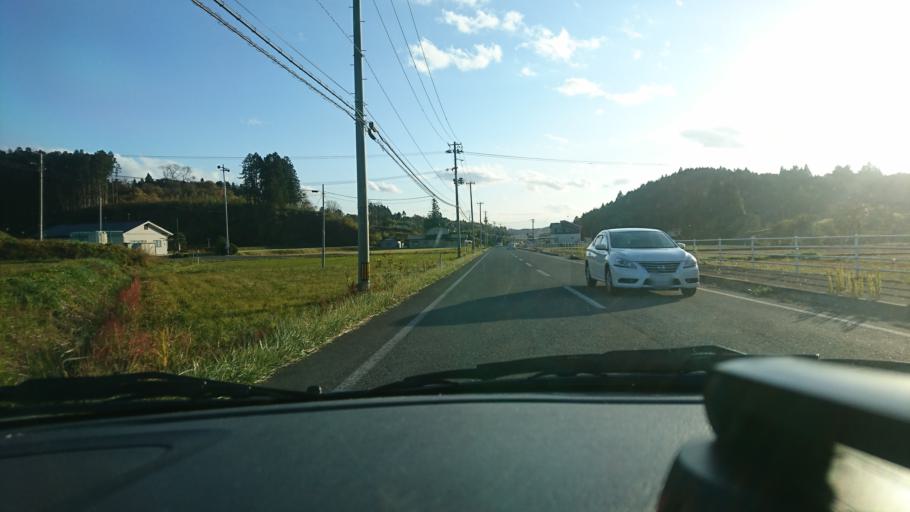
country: JP
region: Iwate
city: Ichinoseki
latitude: 38.8584
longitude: 141.1842
